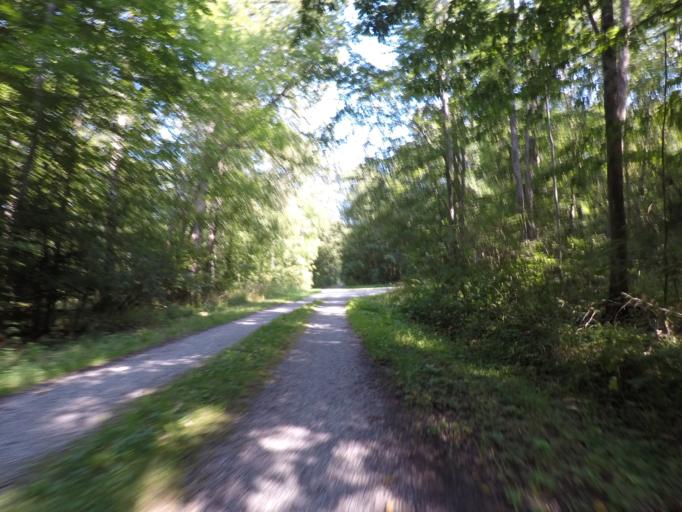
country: DE
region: Baden-Wuerttemberg
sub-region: Regierungsbezirk Stuttgart
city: Ehningen
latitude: 48.6702
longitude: 8.9718
